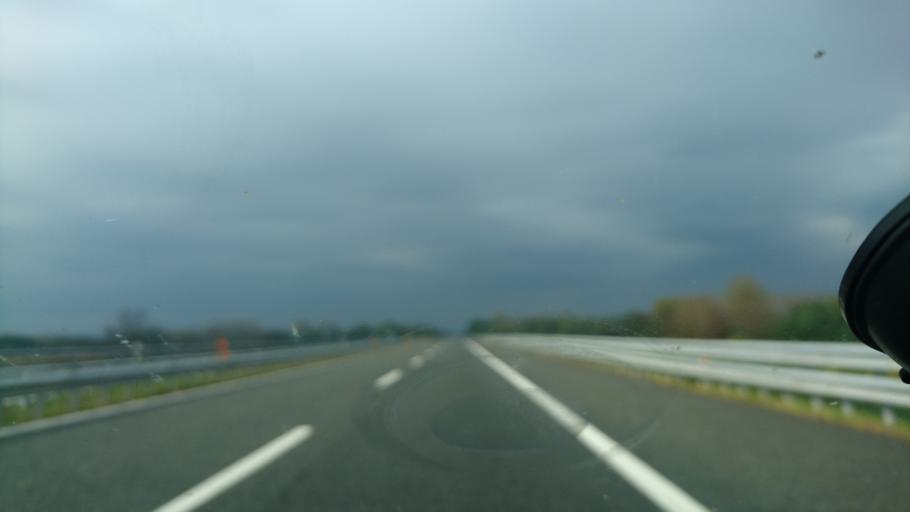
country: IT
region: Piedmont
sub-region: Provincia di Novara
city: Carpignano Sesia
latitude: 45.5395
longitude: 8.4288
